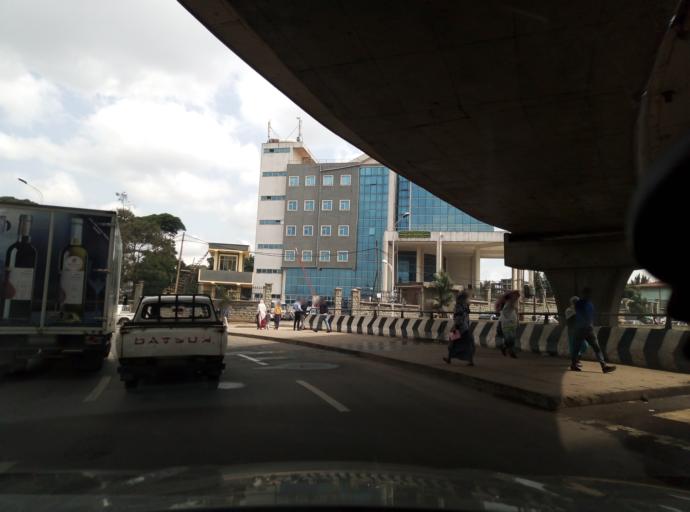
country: ET
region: Adis Abeba
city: Addis Ababa
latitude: 9.0118
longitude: 38.7346
